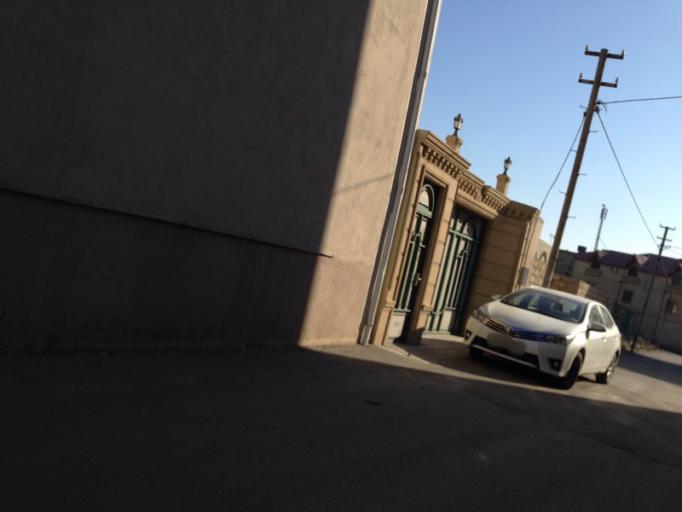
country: AZ
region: Baki
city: Baku
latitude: 40.4212
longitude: 49.8658
